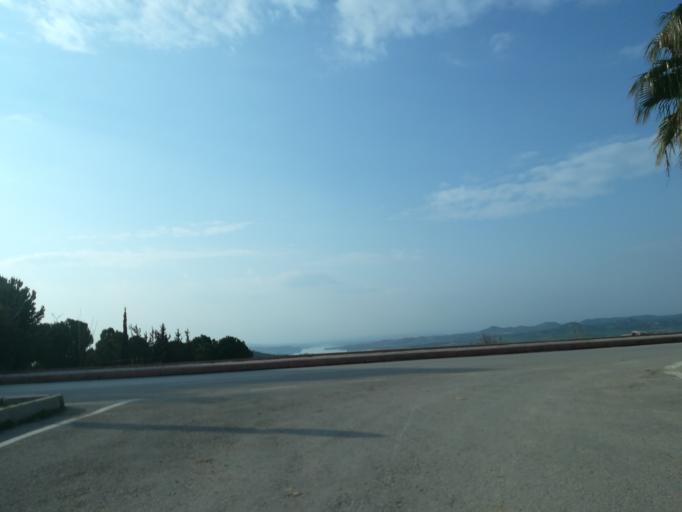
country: TR
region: Adana
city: Adana
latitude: 37.0728
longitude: 35.3827
